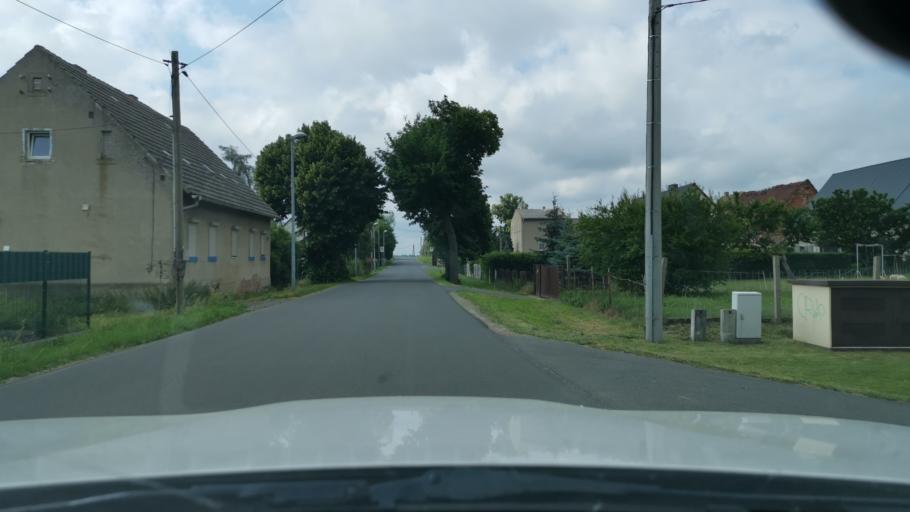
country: DE
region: Saxony
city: Torgau
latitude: 51.6149
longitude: 13.0162
